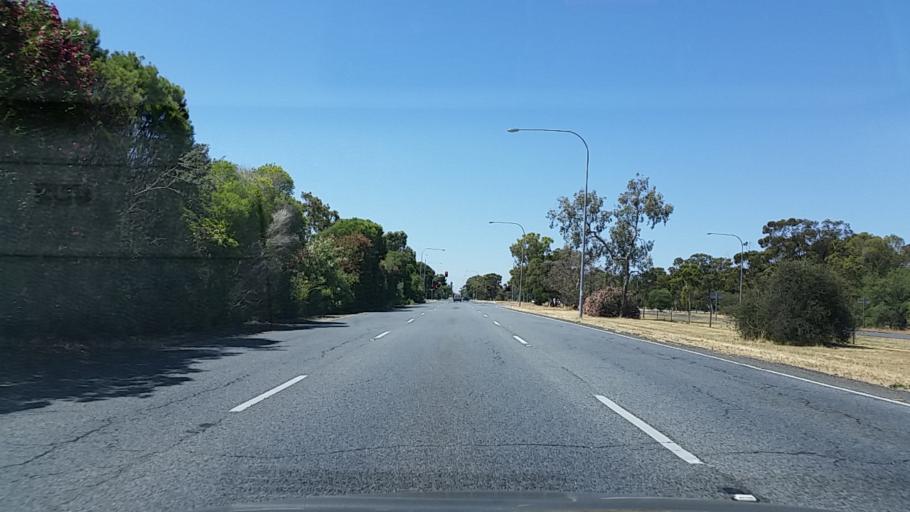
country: AU
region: South Australia
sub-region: Playford
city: Smithfield
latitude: -34.7012
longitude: 138.6821
